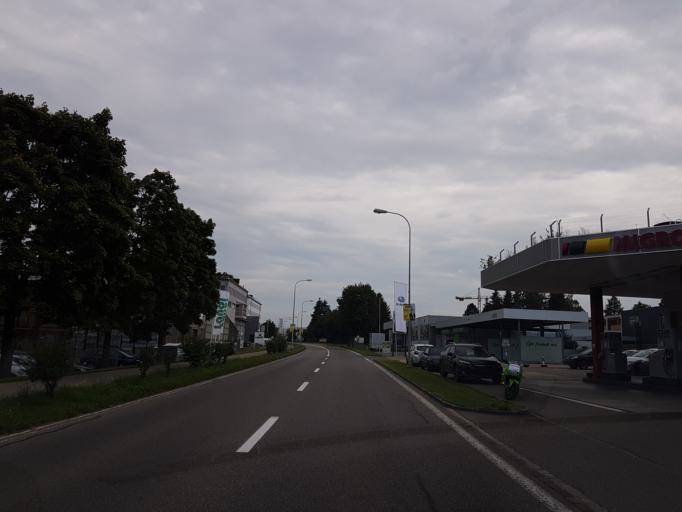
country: CH
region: Aargau
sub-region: Bezirk Muri
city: Muri
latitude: 47.2669
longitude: 8.3477
